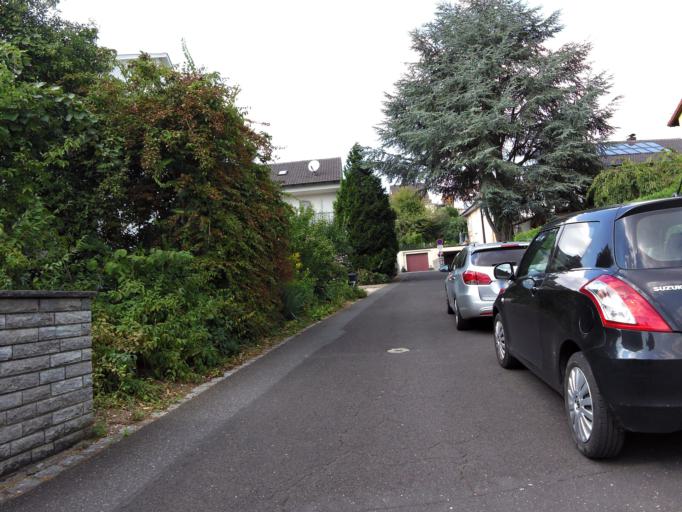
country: DE
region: Bavaria
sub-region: Regierungsbezirk Unterfranken
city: Estenfeld
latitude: 49.8276
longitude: 10.0037
